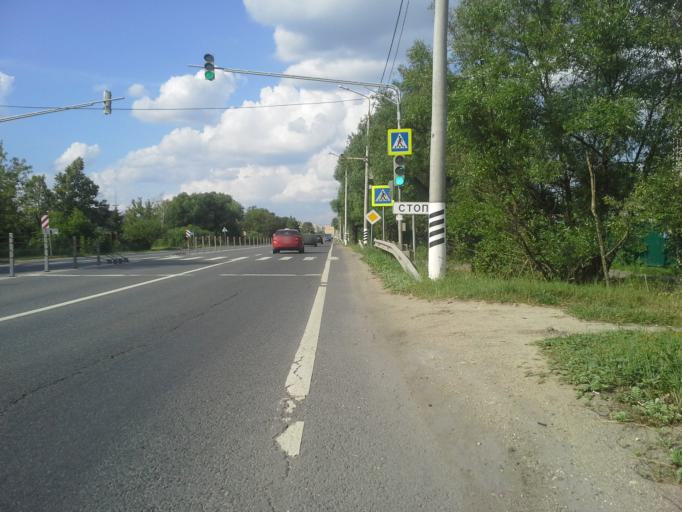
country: RU
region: Moskovskaya
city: Klimovsk
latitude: 55.3491
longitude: 37.5289
